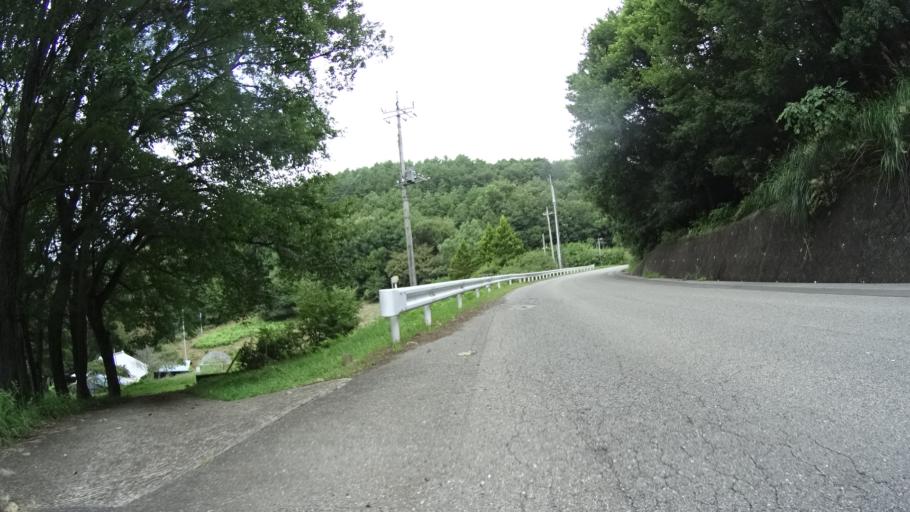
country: JP
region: Yamanashi
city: Nirasaki
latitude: 35.8582
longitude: 138.5212
